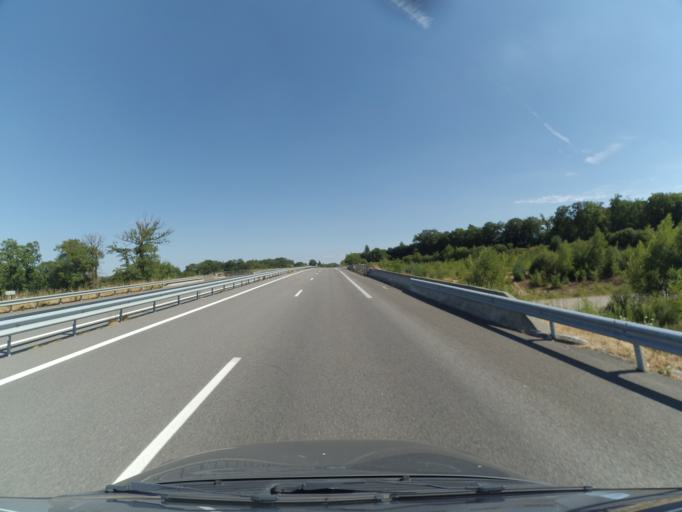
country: FR
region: Limousin
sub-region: Departement de la Haute-Vienne
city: Saint-Victurnien
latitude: 45.8993
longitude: 1.0256
